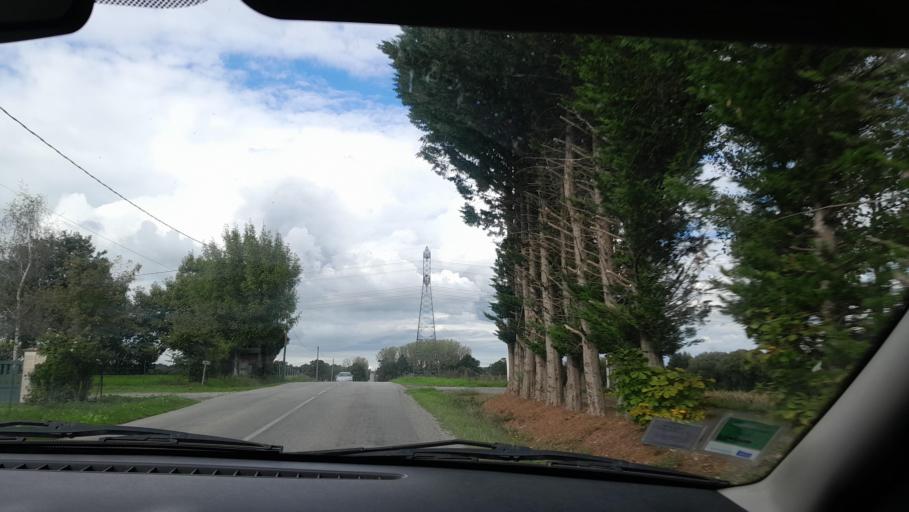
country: FR
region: Brittany
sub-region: Departement d'Ille-et-Vilaine
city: Le Pertre
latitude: 47.9910
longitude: -1.0406
